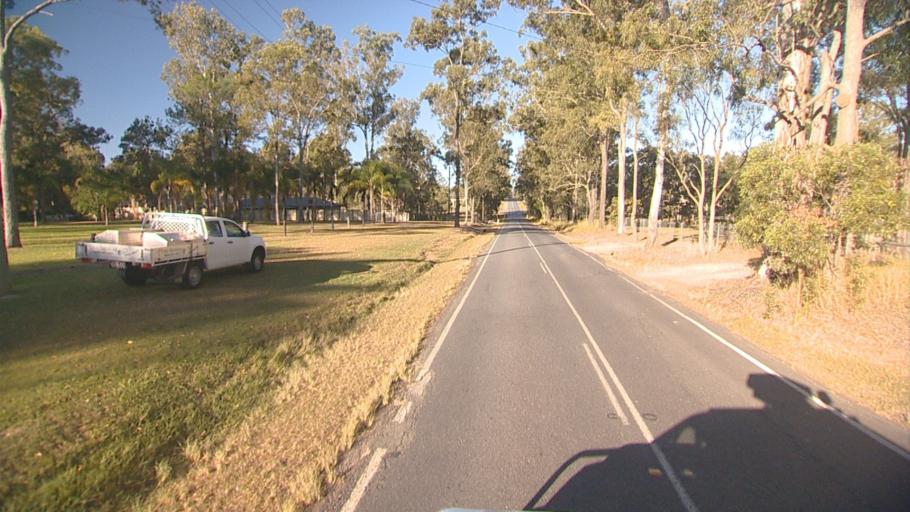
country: AU
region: Queensland
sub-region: Logan
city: North Maclean
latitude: -27.7579
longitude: 153.0312
